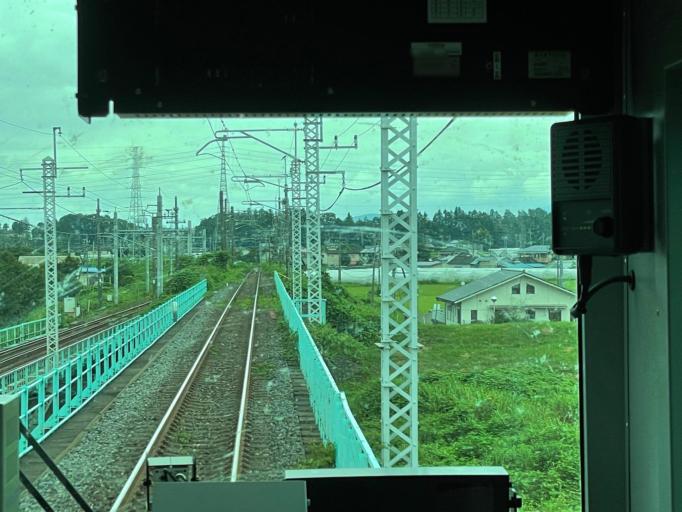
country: JP
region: Tochigi
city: Ujiie
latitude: 36.6111
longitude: 139.9693
